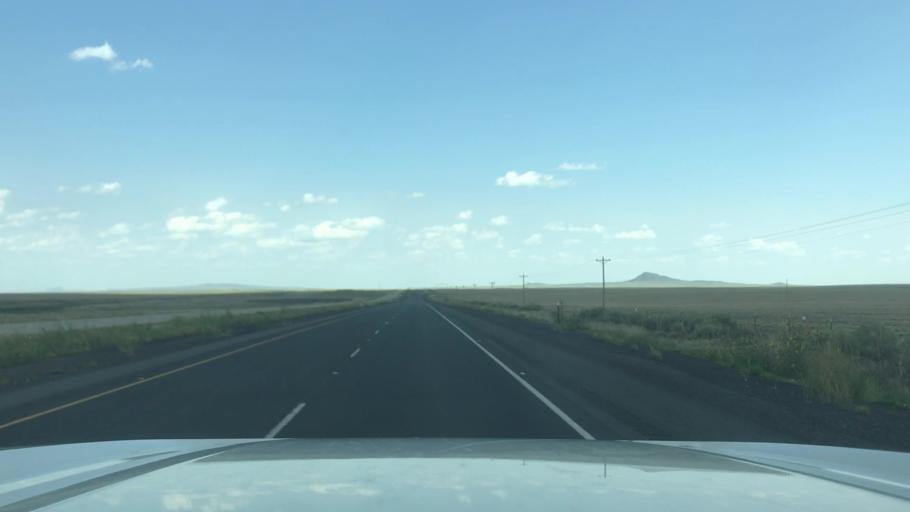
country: US
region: New Mexico
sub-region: Union County
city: Clayton
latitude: 36.6292
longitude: -103.7103
